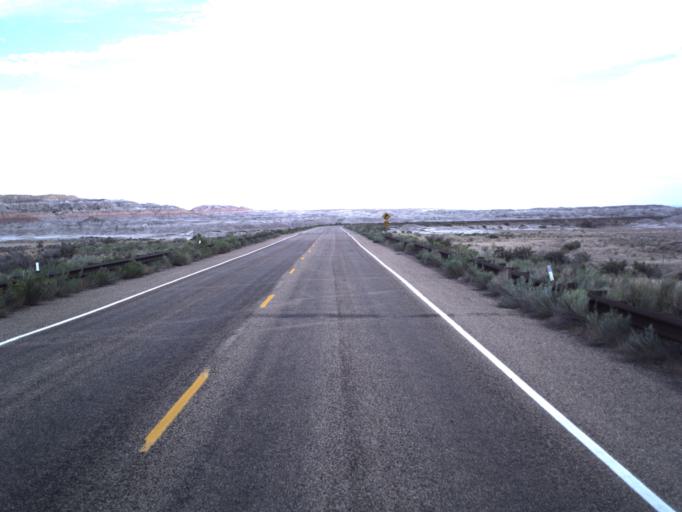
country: US
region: Utah
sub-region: Uintah County
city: Naples
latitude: 40.1111
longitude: -109.2330
